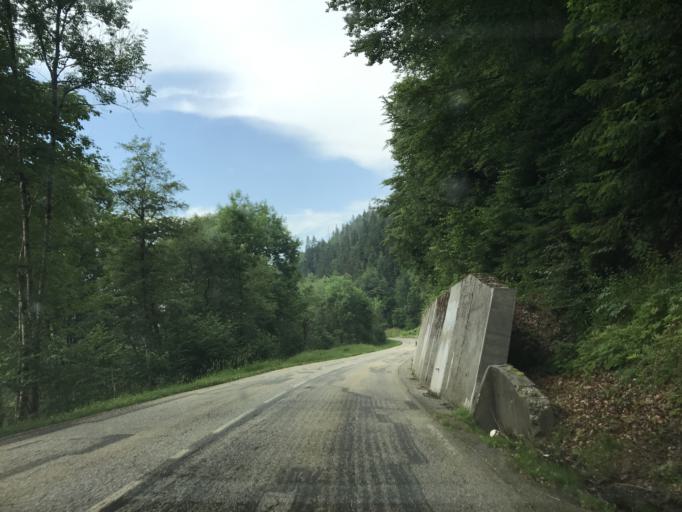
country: FR
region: Rhone-Alpes
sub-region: Departement de l'Isere
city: Allevard
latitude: 45.3308
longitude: 6.0918
